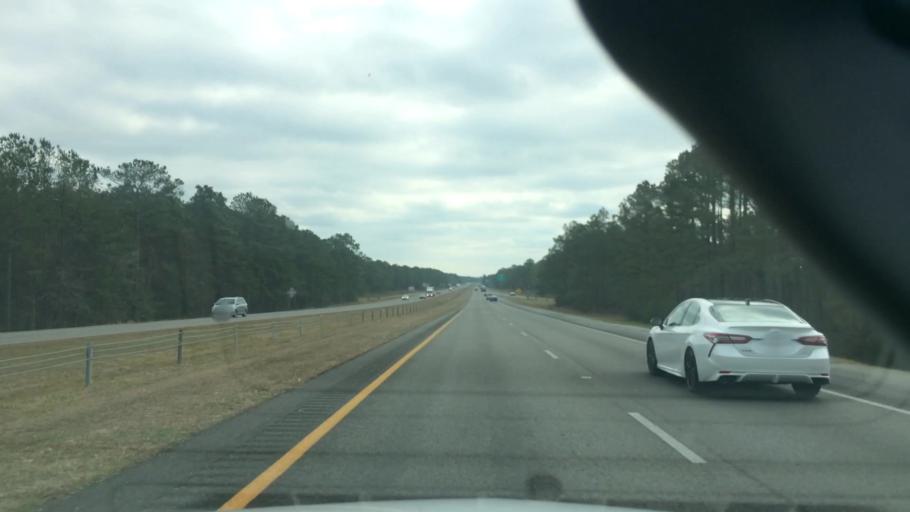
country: US
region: North Carolina
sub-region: New Hanover County
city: Castle Hayne
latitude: 34.3518
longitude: -77.8845
